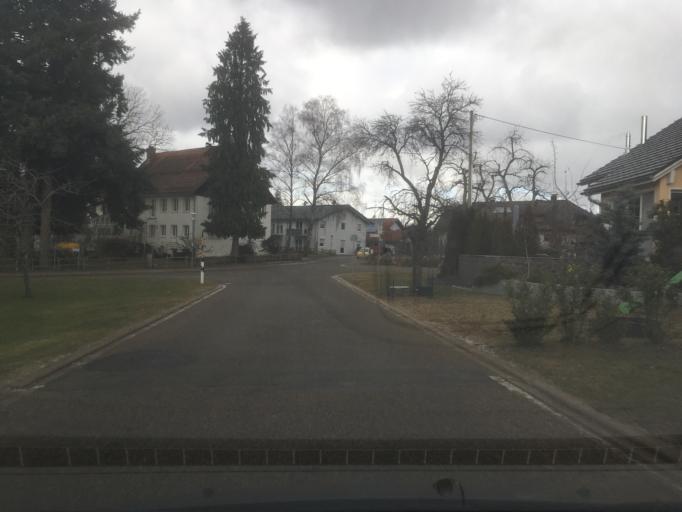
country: DE
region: Baden-Wuerttemberg
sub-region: Freiburg Region
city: Hochenschwand
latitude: 47.6895
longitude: 8.1460
